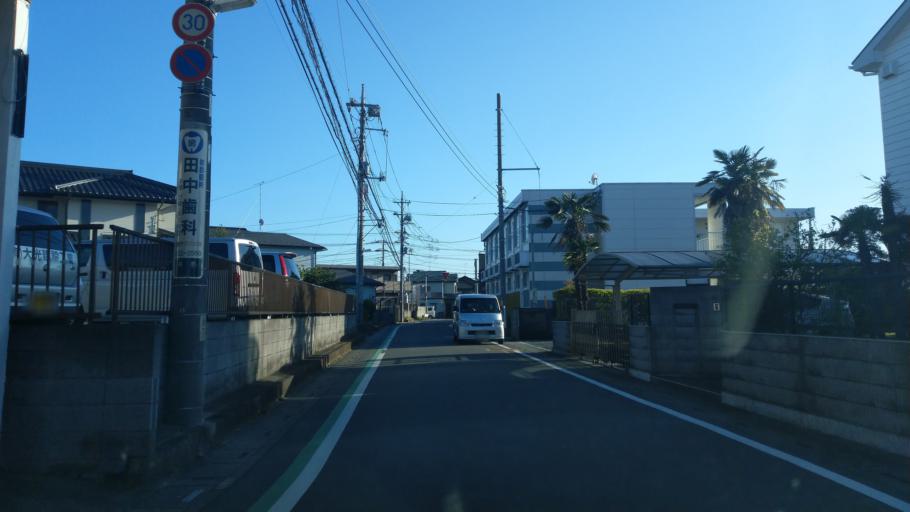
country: JP
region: Saitama
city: Yono
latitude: 35.9148
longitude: 139.5736
